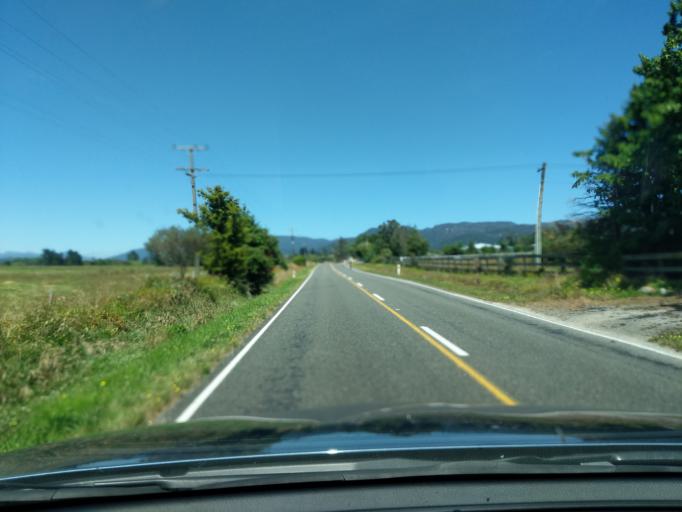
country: NZ
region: Tasman
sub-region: Tasman District
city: Takaka
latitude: -40.6849
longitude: 172.6575
